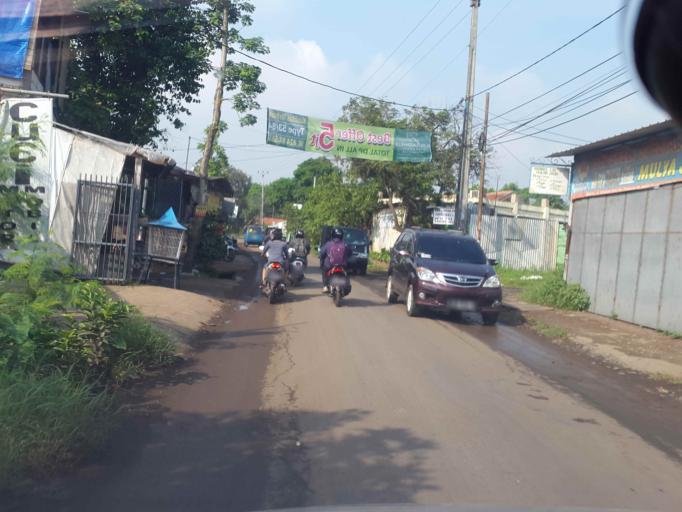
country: ID
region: West Java
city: Cileungsir
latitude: -6.3783
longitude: 106.9953
